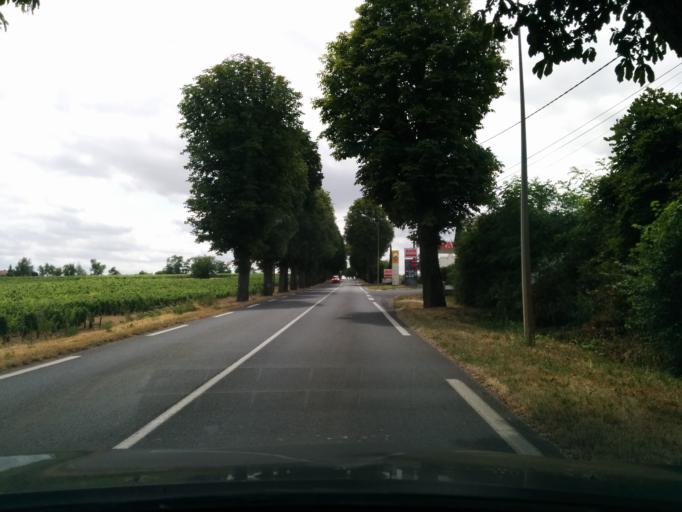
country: FR
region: Centre
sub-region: Departement du Cher
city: Sancerre
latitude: 47.3250
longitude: 2.8250
